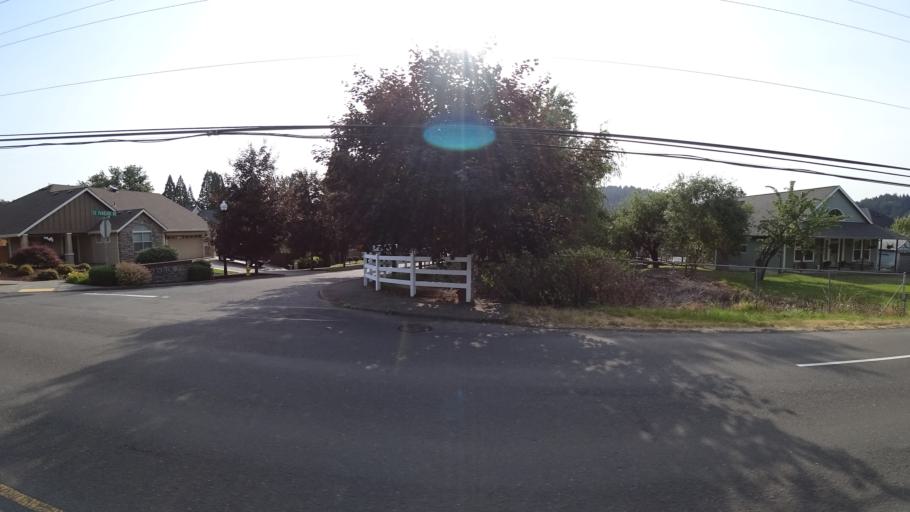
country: US
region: Oregon
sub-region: Clackamas County
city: Happy Valley
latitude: 45.4507
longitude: -122.5276
